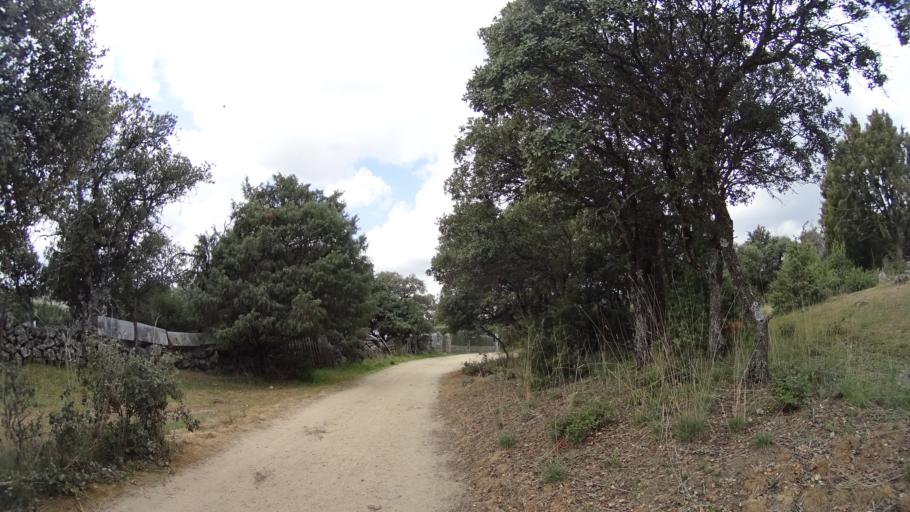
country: ES
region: Madrid
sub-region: Provincia de Madrid
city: Hoyo de Manzanares
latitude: 40.6178
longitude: -3.8961
